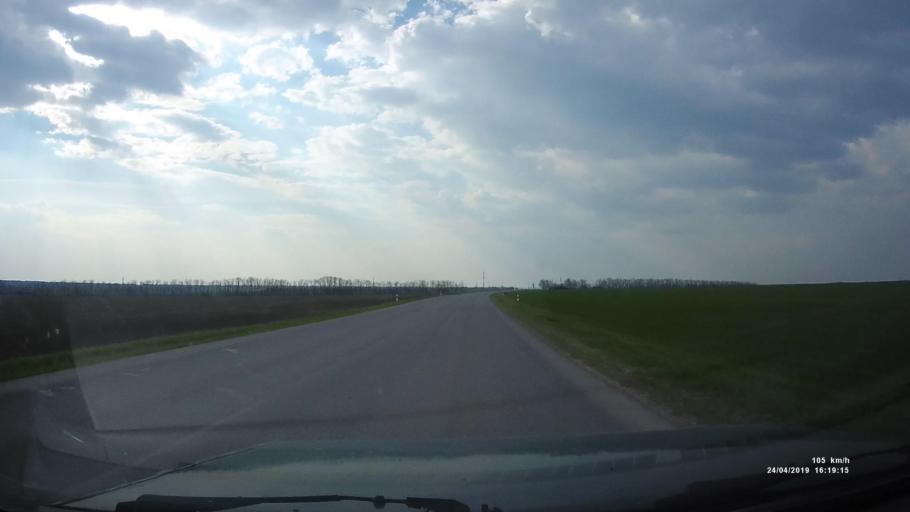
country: RU
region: Rostov
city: Sovetskoye
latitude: 46.7797
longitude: 42.0994
